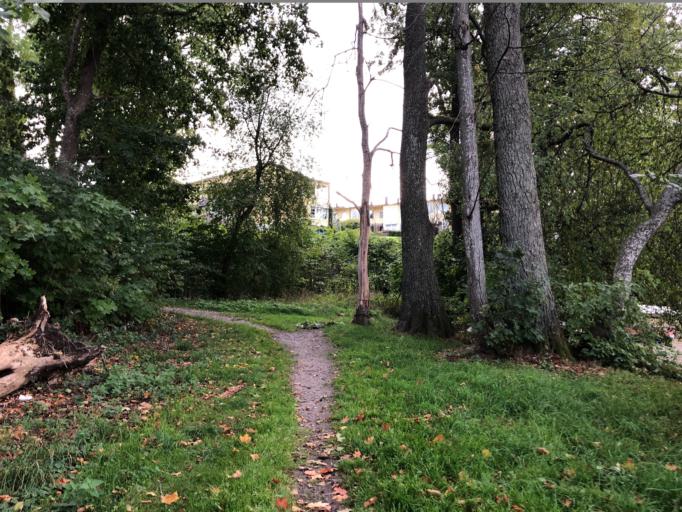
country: SE
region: Stockholm
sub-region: Tyreso Kommun
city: Bollmora
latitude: 59.2074
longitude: 18.1915
